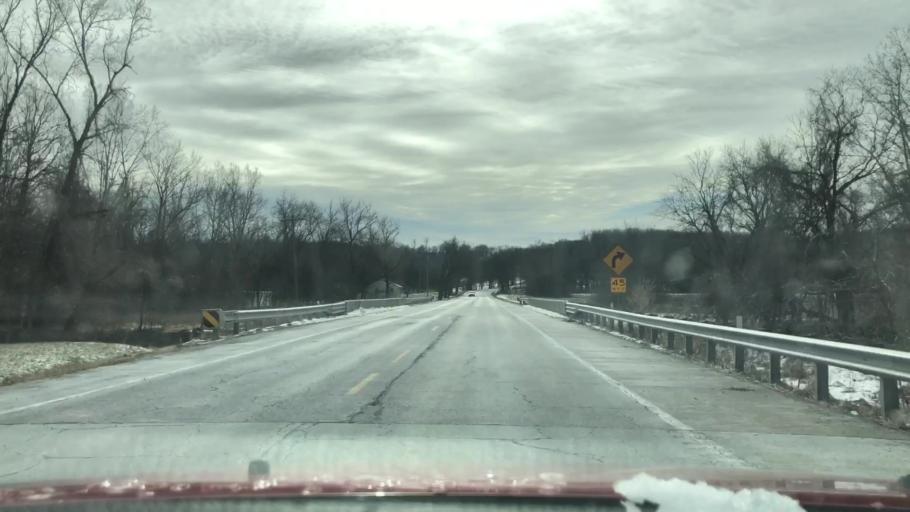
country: US
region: Missouri
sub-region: Jackson County
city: Oak Grove
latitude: 38.9441
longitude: -94.1320
